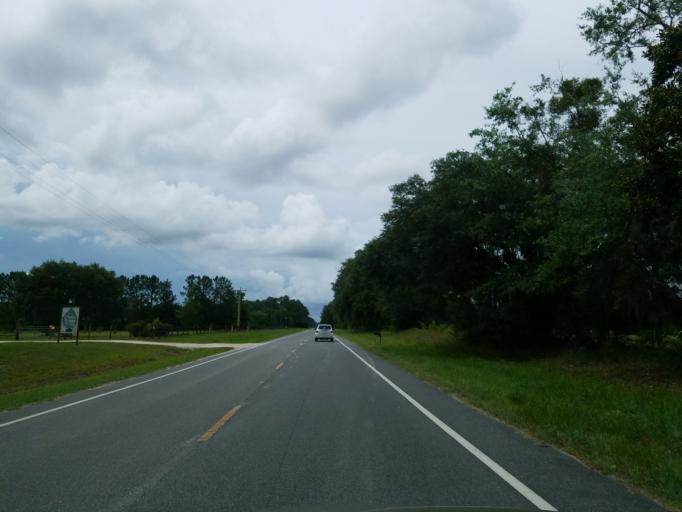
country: US
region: Florida
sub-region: Alachua County
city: High Springs
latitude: 29.8951
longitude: -82.4958
